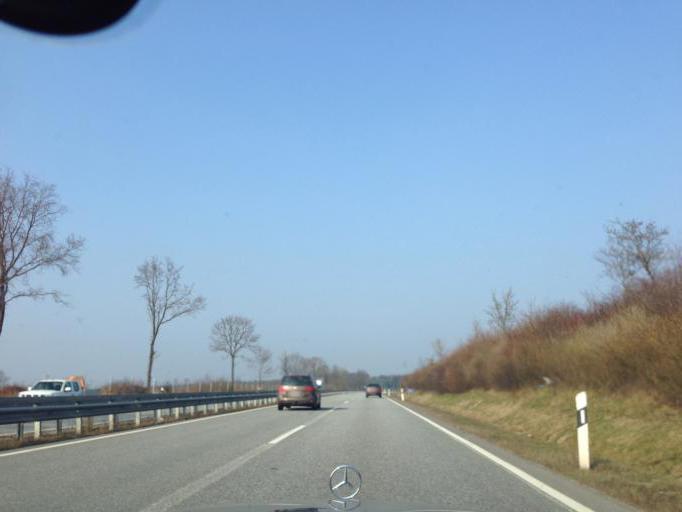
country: DE
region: Schleswig-Holstein
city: Negernbotel
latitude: 53.9820
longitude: 10.2388
